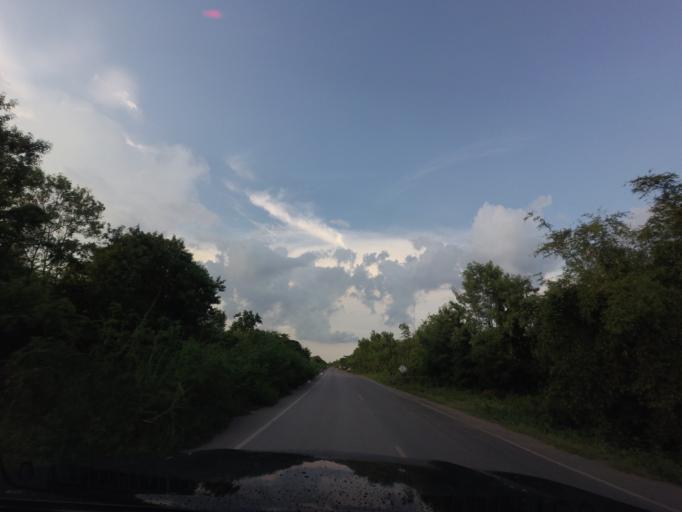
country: TH
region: Khon Kaen
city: Khon Kaen
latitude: 16.4046
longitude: 102.8645
